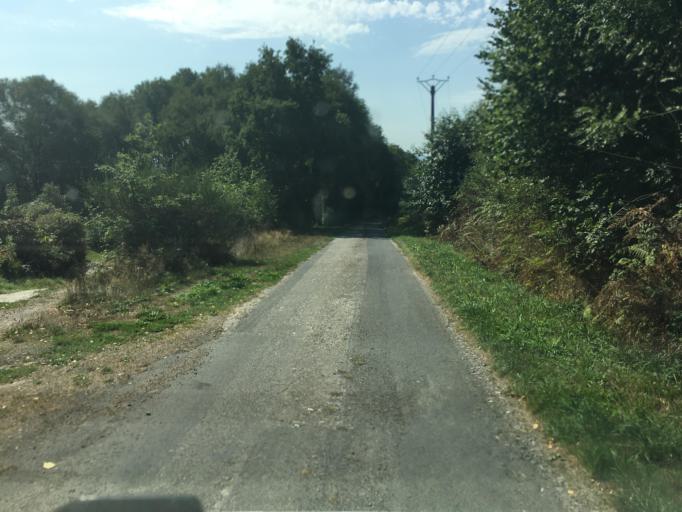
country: FR
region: Brittany
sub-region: Departement des Cotes-d'Armor
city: Mur-de-Bretagne
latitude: 48.2212
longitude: -3.0152
